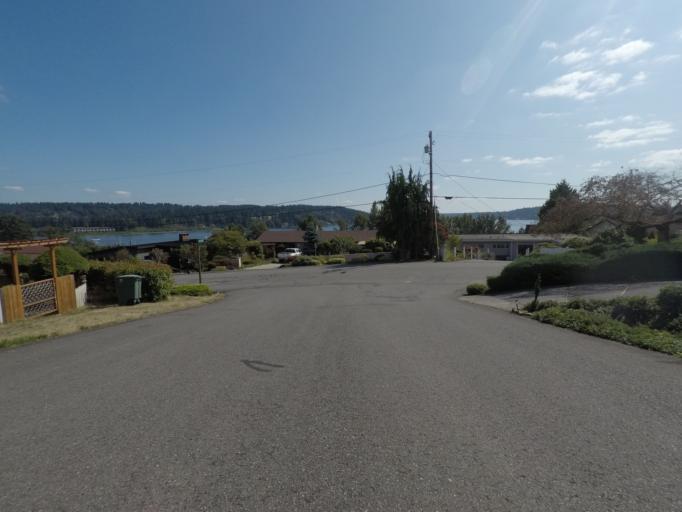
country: US
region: Washington
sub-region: King County
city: Lake Forest Park
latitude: 47.7591
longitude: -122.2668
